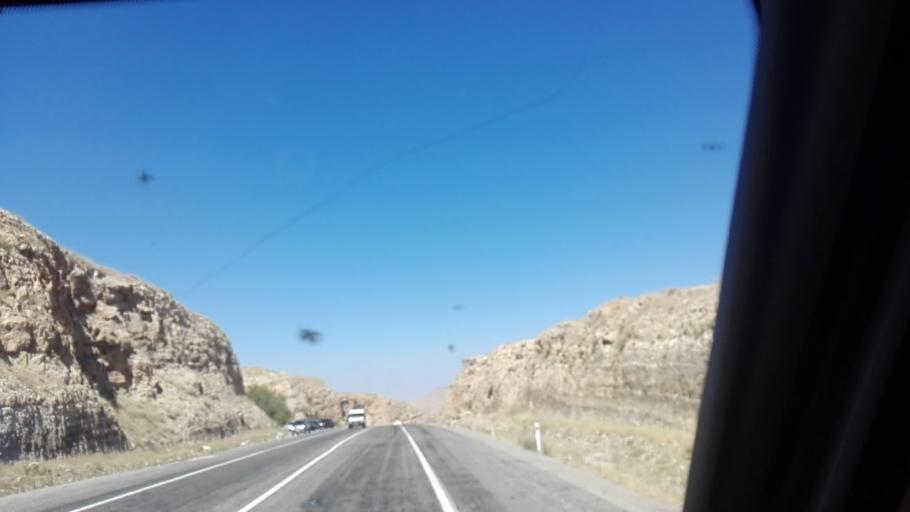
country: TR
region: Batman
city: Gerdzhyush
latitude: 37.5585
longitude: 41.3620
